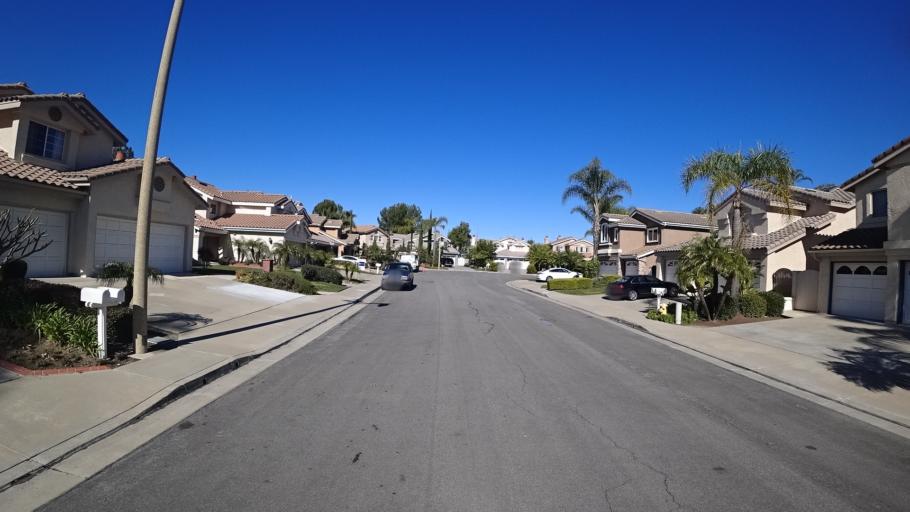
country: US
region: California
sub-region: Orange County
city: Villa Park
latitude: 33.8464
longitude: -117.7404
